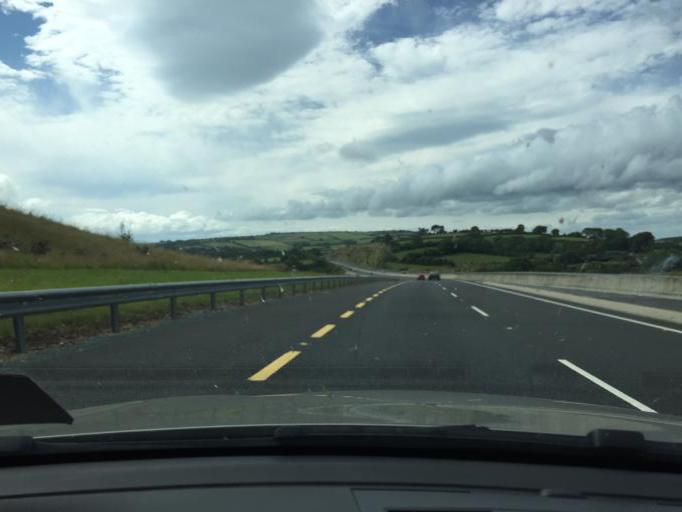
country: IE
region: Leinster
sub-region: Kilkenny
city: Mooncoin
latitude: 52.2366
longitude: -7.2343
